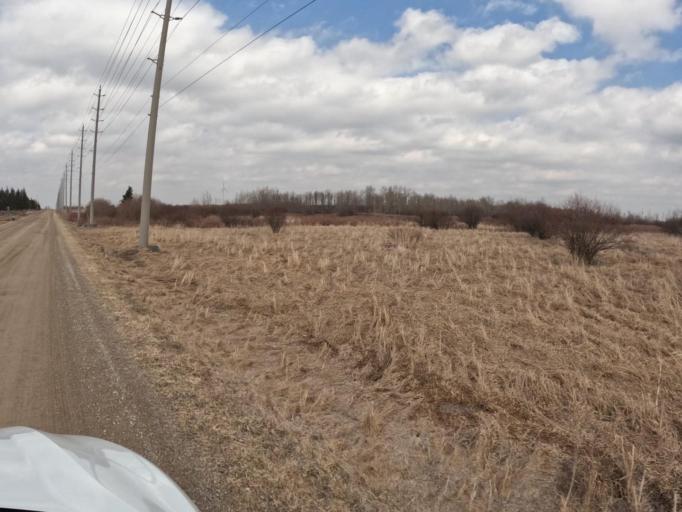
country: CA
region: Ontario
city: Shelburne
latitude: 44.0259
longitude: -80.3141
